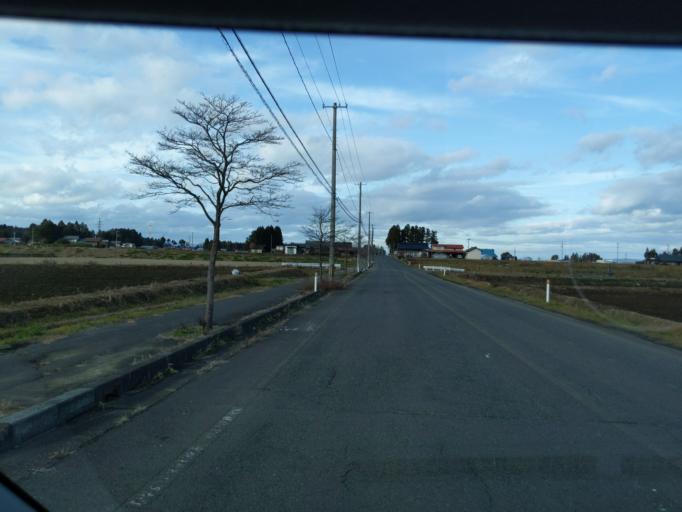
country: JP
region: Iwate
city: Mizusawa
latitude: 39.1205
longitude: 141.0926
